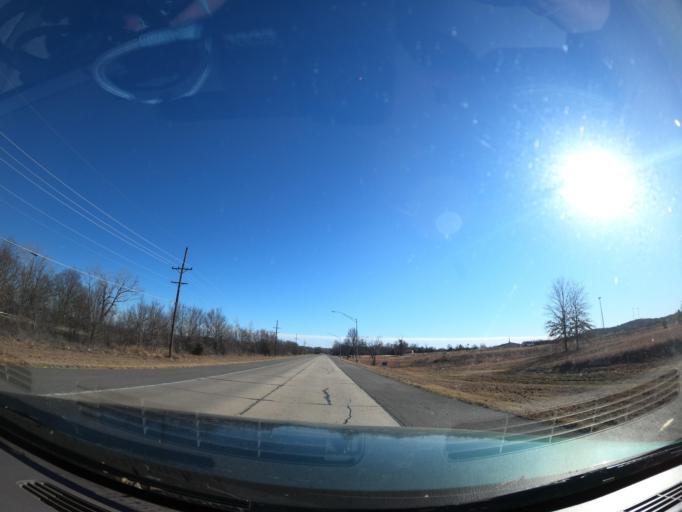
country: US
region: Oklahoma
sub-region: McIntosh County
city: Eufaula
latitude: 35.3020
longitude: -95.5852
